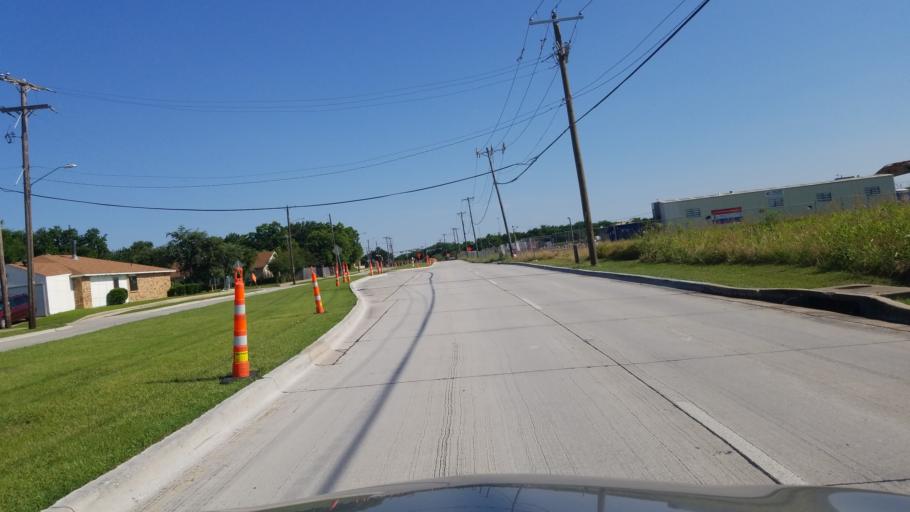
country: US
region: Texas
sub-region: Dallas County
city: Grand Prairie
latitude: 32.6841
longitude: -97.0192
